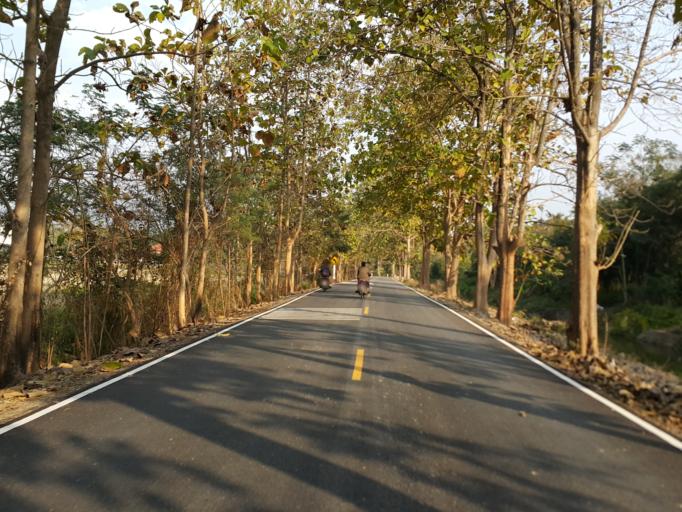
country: TH
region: Chiang Mai
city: San Sai
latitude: 18.8748
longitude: 99.1427
